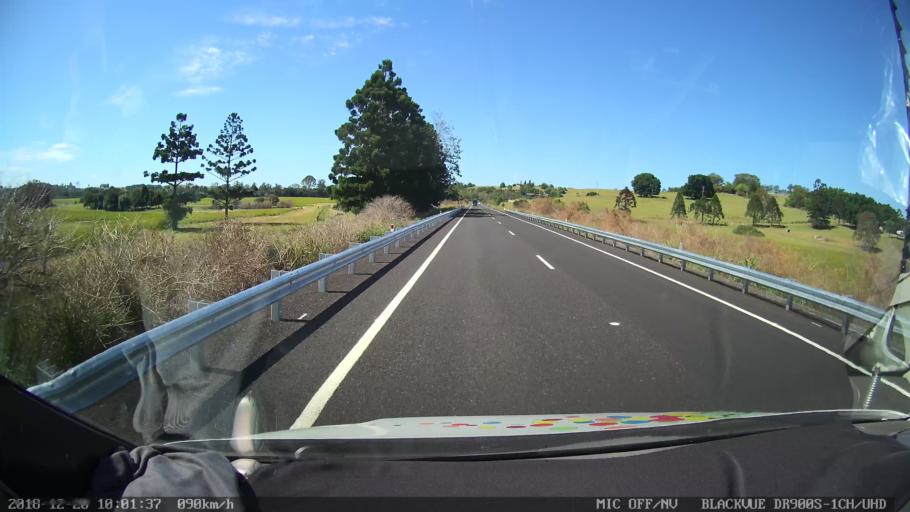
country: AU
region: New South Wales
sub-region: Lismore Municipality
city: Lismore
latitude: -28.8469
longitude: 153.2620
